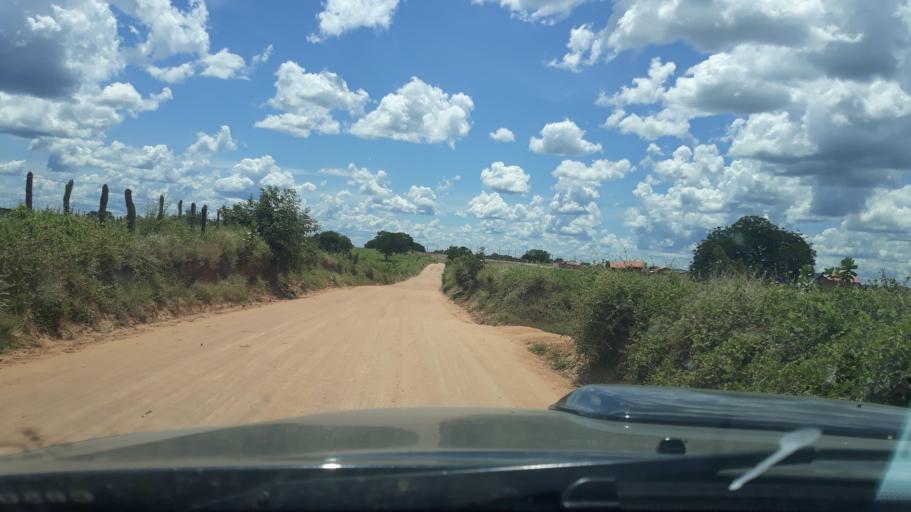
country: BR
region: Bahia
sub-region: Riacho De Santana
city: Riacho de Santana
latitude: -13.9083
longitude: -42.8528
